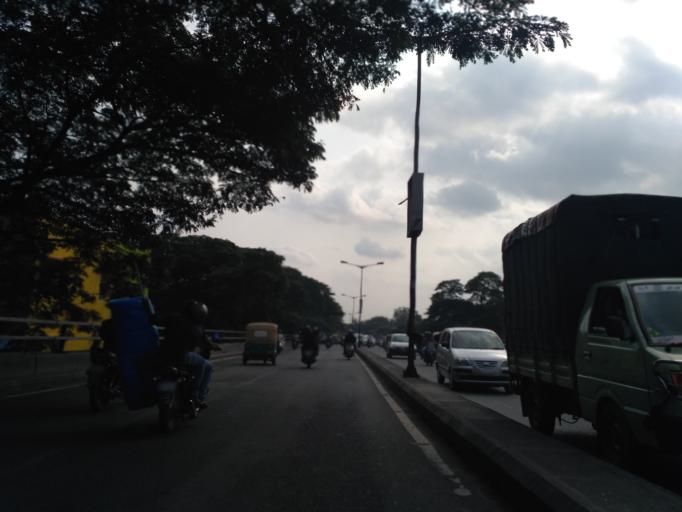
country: IN
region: Karnataka
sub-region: Bangalore Urban
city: Bangalore
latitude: 12.9615
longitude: 77.5603
